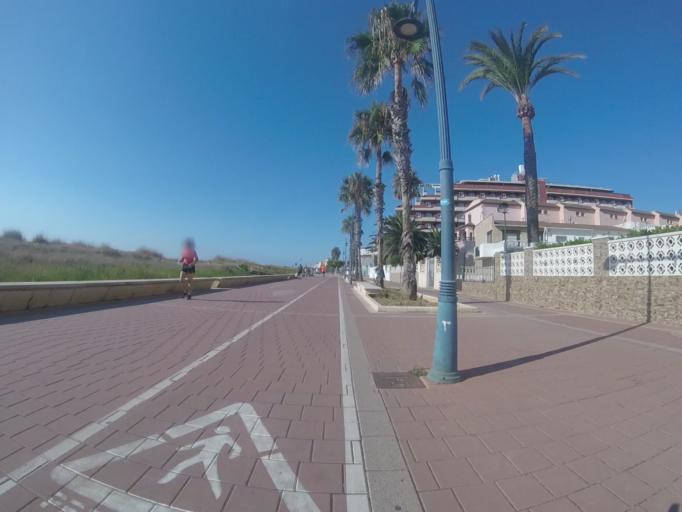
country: ES
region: Valencia
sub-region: Provincia de Castello
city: Peniscola
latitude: 40.3866
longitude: 0.4104
